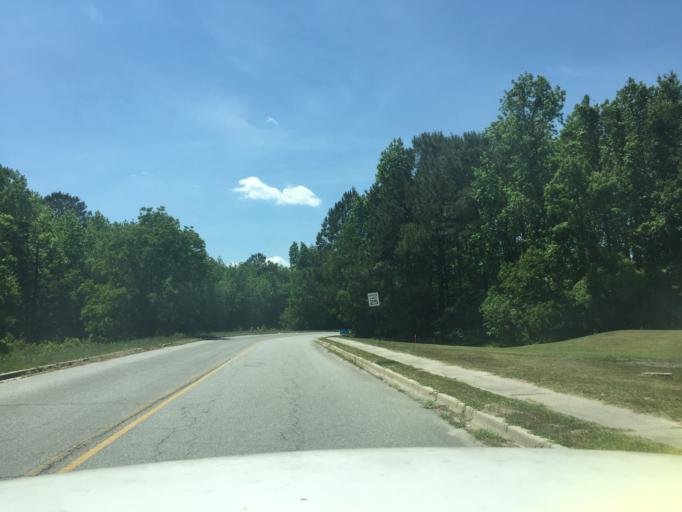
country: US
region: Georgia
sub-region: Chatham County
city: Georgetown
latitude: 32.0035
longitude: -81.2723
